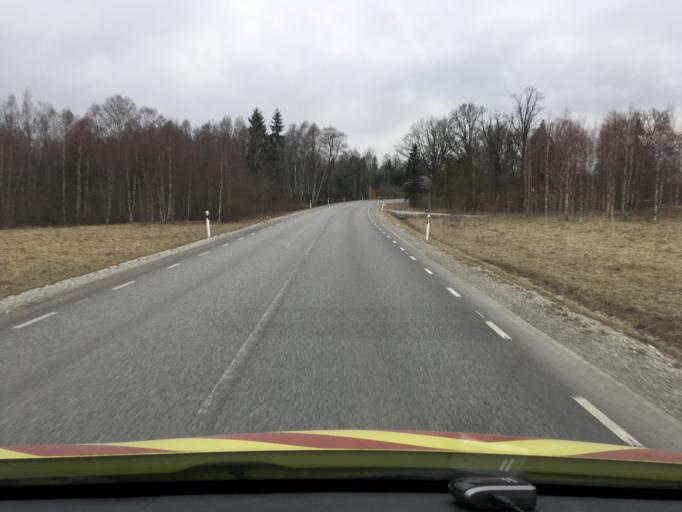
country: EE
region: Raplamaa
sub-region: Rapla vald
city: Rapla
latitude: 58.9982
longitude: 24.8443
